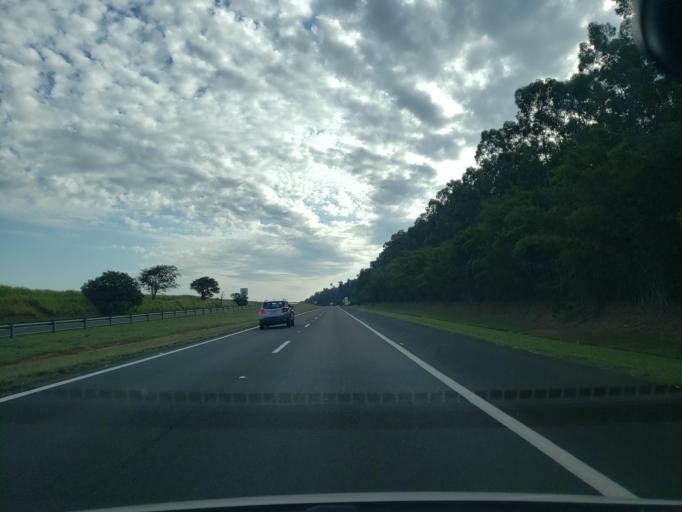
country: BR
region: Sao Paulo
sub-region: Guararapes
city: Guararapes
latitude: -21.2000
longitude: -50.5619
